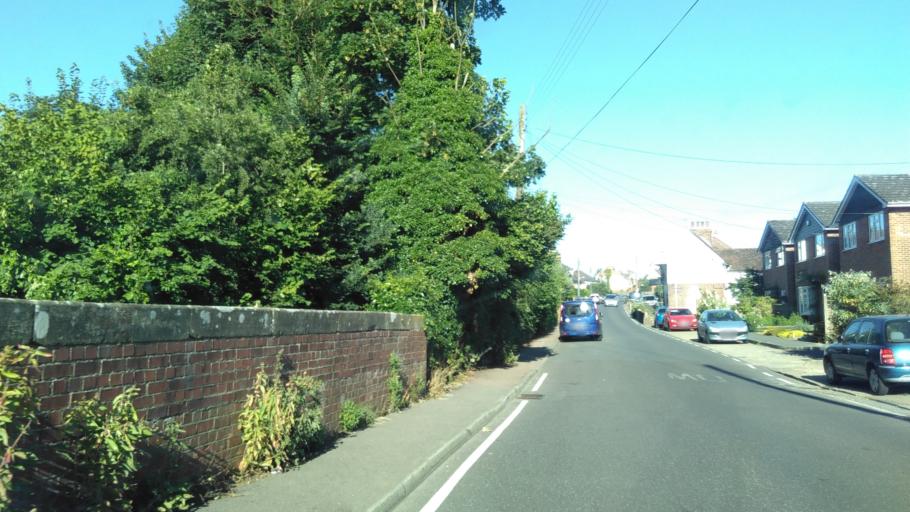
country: GB
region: England
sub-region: Kent
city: Chartham
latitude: 51.2533
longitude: 1.0022
